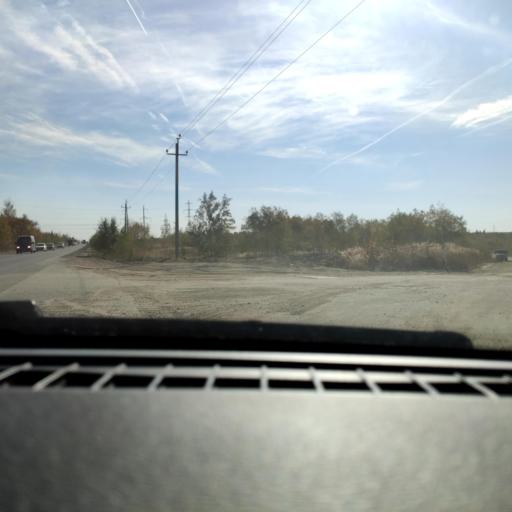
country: RU
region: Voronezj
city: Maslovka
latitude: 51.5845
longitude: 39.2575
